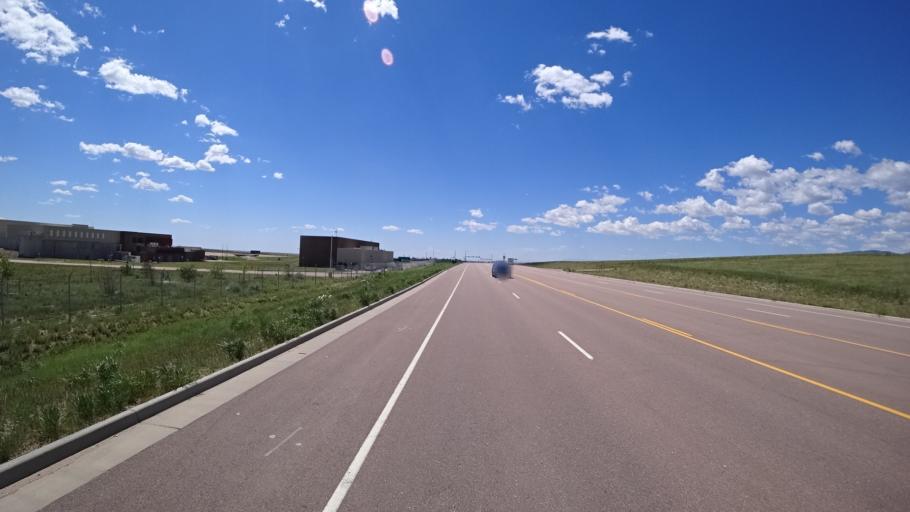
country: US
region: Colorado
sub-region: El Paso County
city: Cimarron Hills
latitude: 38.8451
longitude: -104.6828
